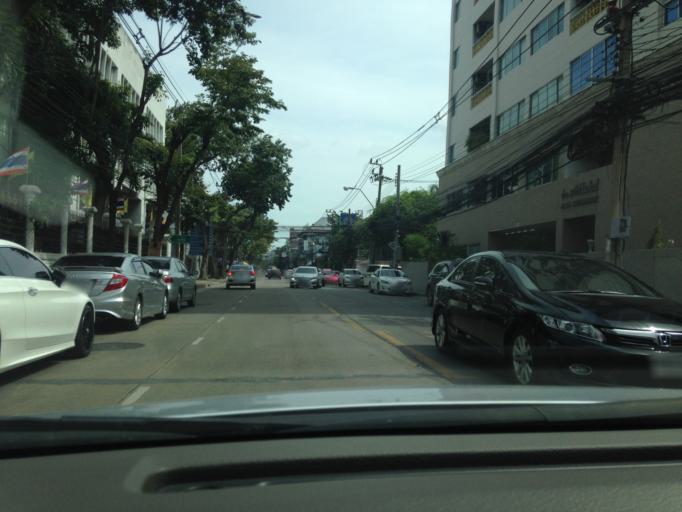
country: TH
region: Bangkok
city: Phaya Thai
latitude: 13.7802
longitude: 100.5361
